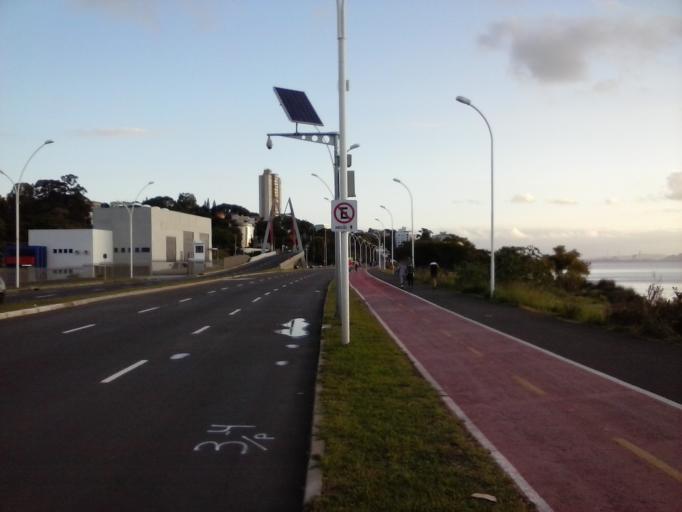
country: BR
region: Rio Grande do Sul
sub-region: Porto Alegre
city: Porto Alegre
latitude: -30.0716
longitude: -51.2409
